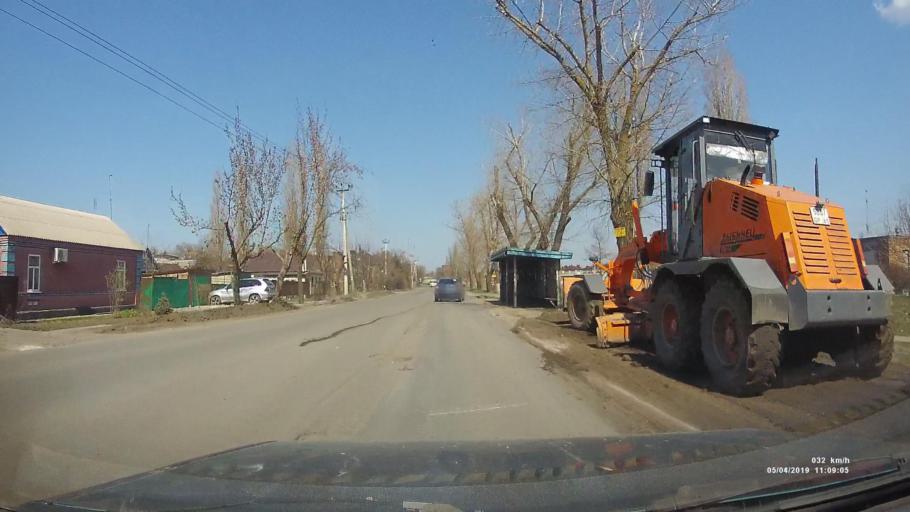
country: RU
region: Rostov
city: Azov
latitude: 47.0888
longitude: 39.4337
